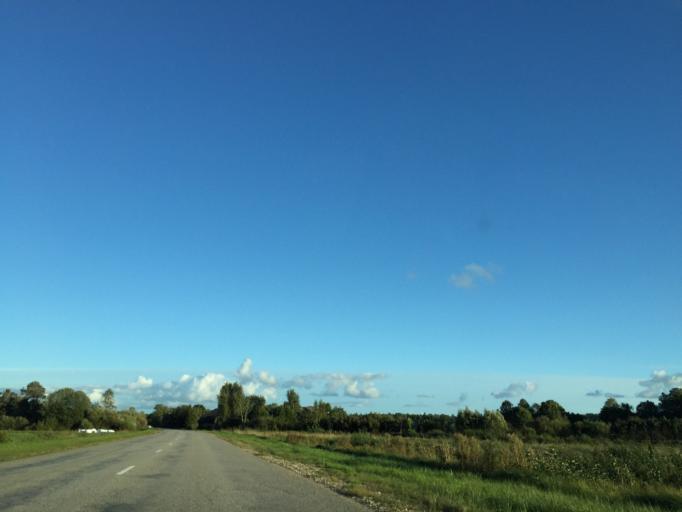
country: LV
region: Kuldigas Rajons
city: Kuldiga
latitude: 56.9370
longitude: 22.0296
